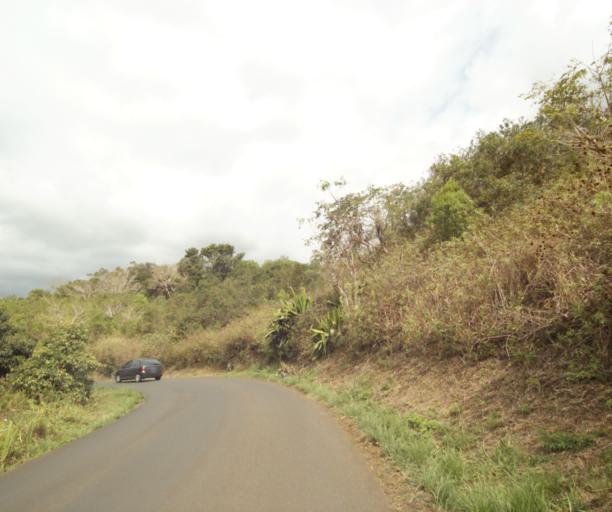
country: RE
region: Reunion
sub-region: Reunion
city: Saint-Paul
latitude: -21.0331
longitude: 55.2922
